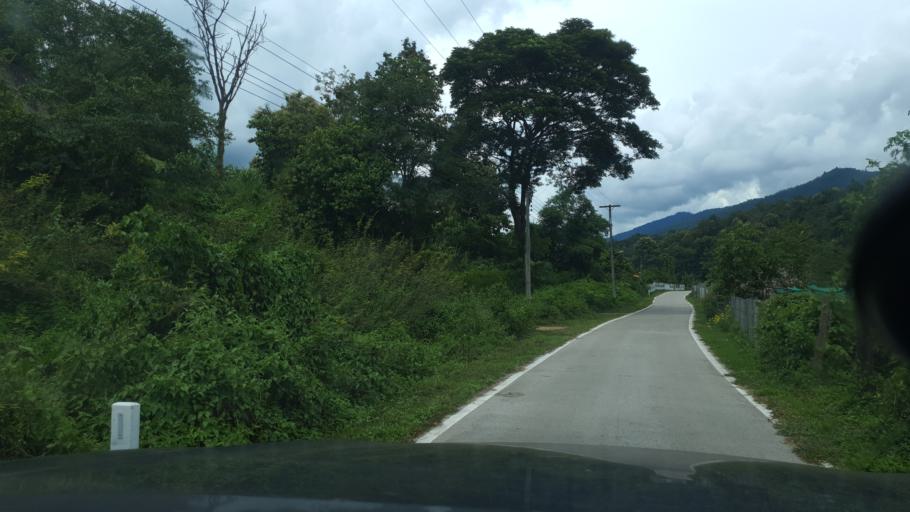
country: TH
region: Lampang
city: Hang Chat
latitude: 18.4300
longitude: 99.2676
